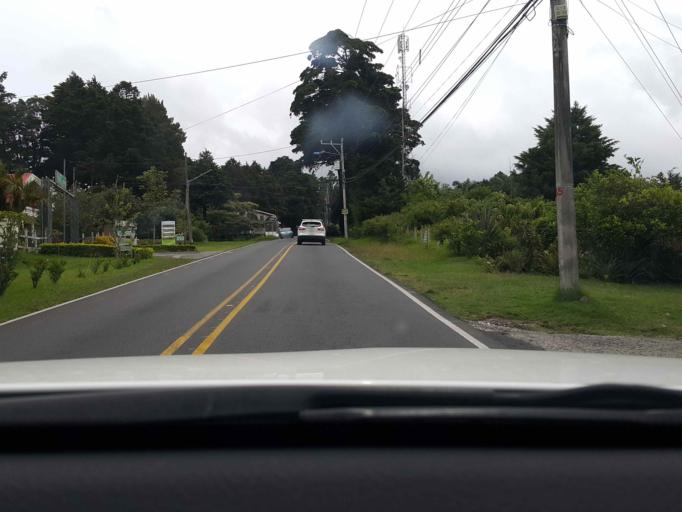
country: CR
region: Heredia
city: San Josecito
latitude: 10.0475
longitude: -84.0887
